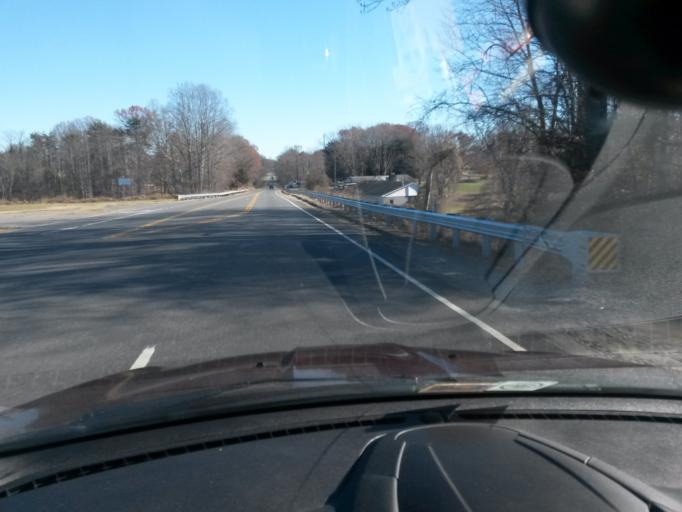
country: US
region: Virginia
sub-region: Henry County
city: Bassett
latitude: 36.7605
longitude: -80.0490
